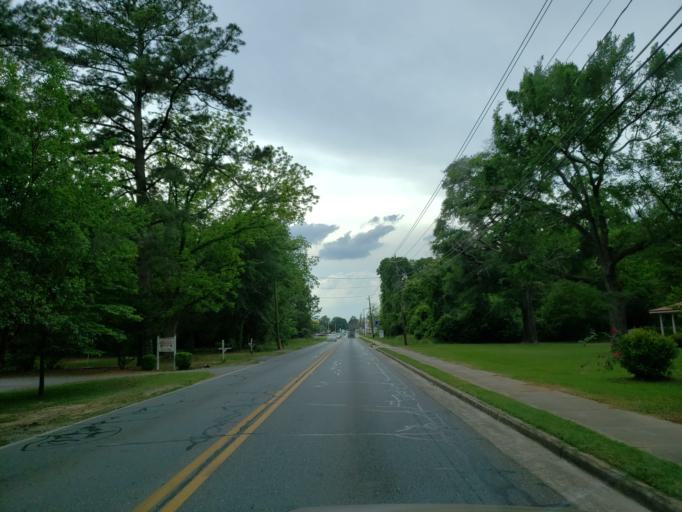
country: US
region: Georgia
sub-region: Macon County
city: Montezuma
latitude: 32.2935
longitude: -84.0146
